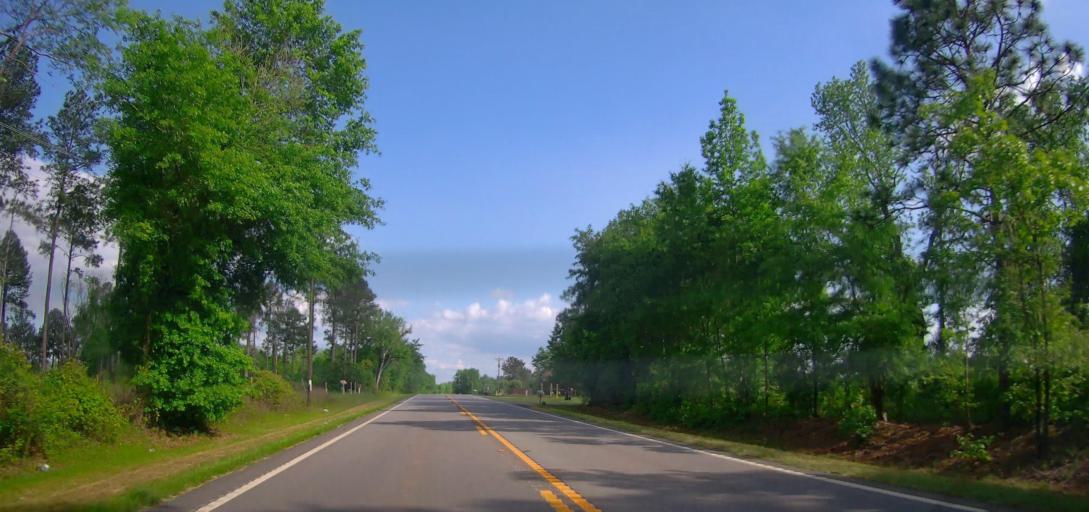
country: US
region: Georgia
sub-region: Baldwin County
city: Hardwick
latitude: 33.0445
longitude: -83.1185
